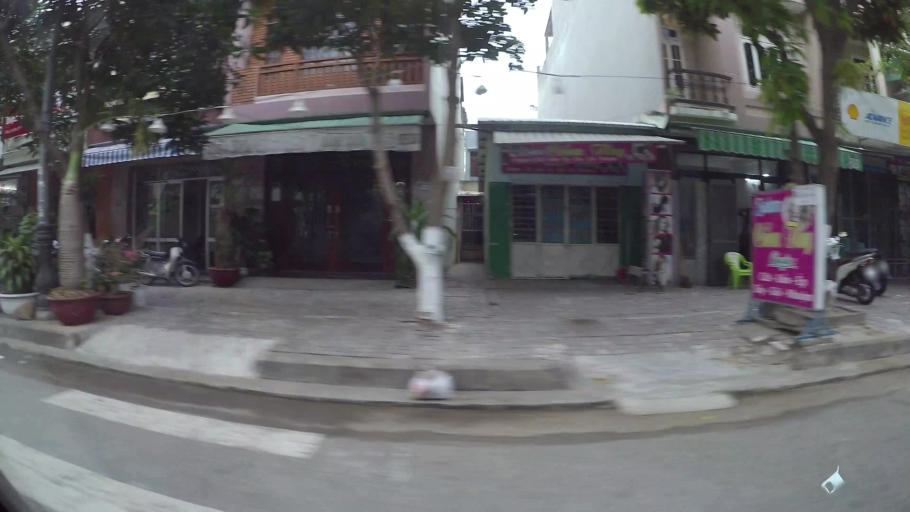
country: VN
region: Da Nang
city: Da Nang
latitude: 16.0867
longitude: 108.2392
